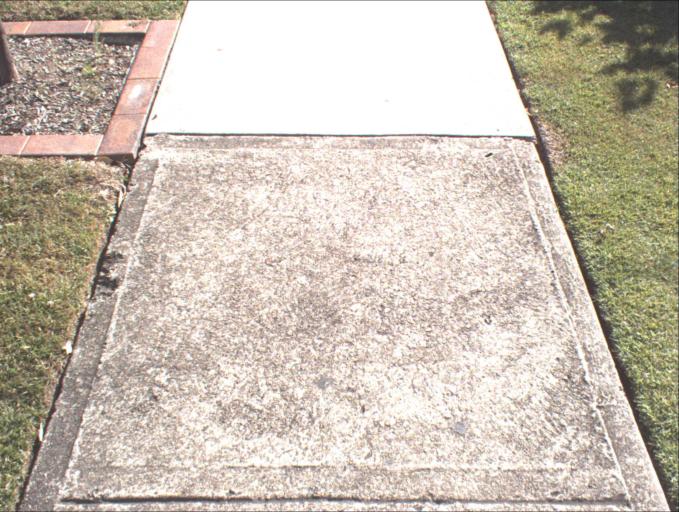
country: AU
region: Queensland
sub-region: Logan
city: Beenleigh
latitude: -27.7182
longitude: 153.1991
